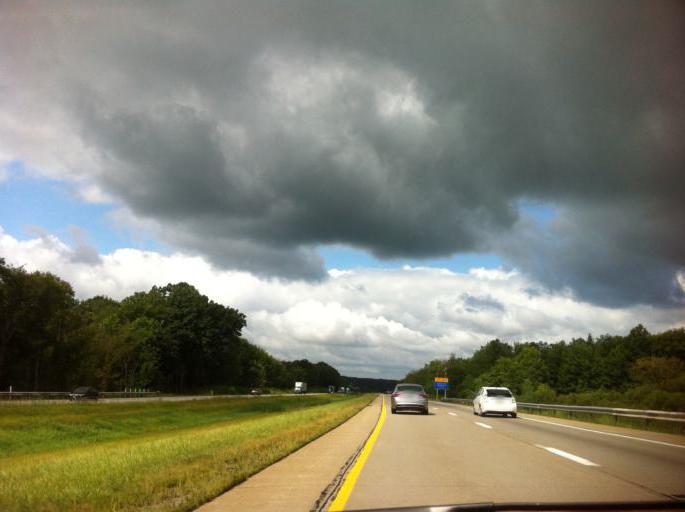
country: US
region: Pennsylvania
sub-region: Lawrence County
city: New Wilmington
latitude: 41.1854
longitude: -80.3687
